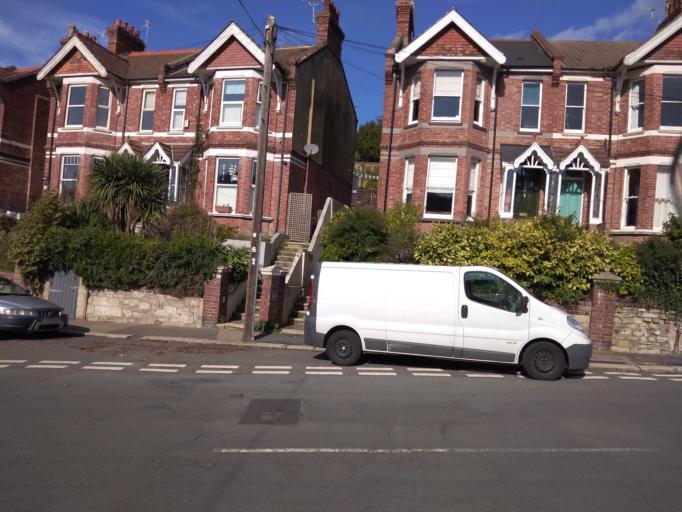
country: GB
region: England
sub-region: East Sussex
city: Hastings
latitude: 50.8637
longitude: 0.6024
